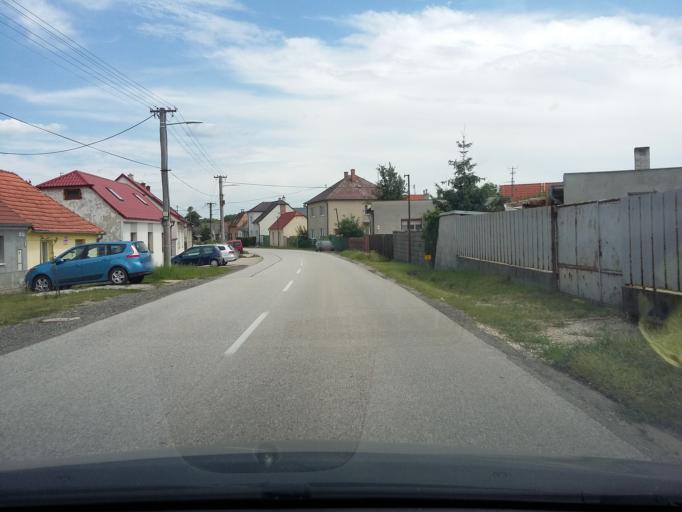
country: SK
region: Bratislavsky
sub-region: Okres Malacky
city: Malacky
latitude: 48.4413
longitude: 17.0387
